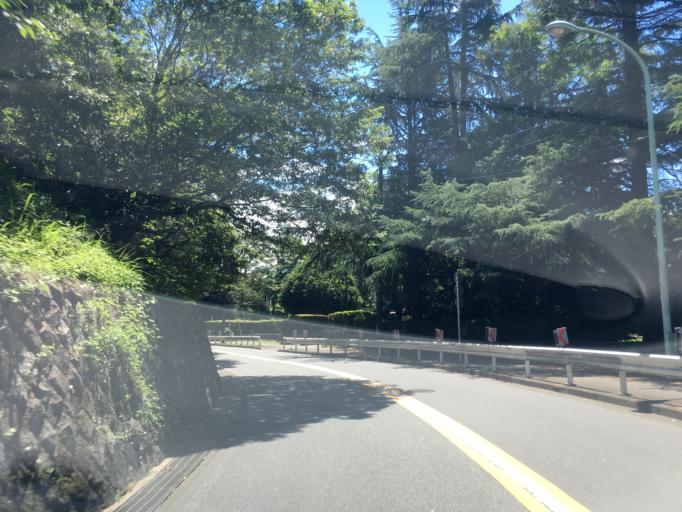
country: JP
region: Tokyo
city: Kokubunji
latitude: 35.6362
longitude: 139.4639
